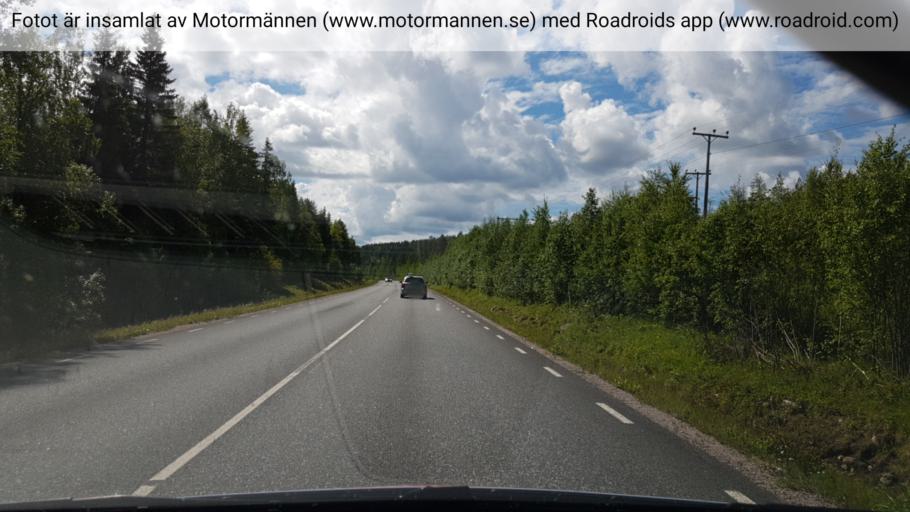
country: FI
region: Lapland
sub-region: Torniolaakso
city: Ylitornio
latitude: 66.3229
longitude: 23.6221
